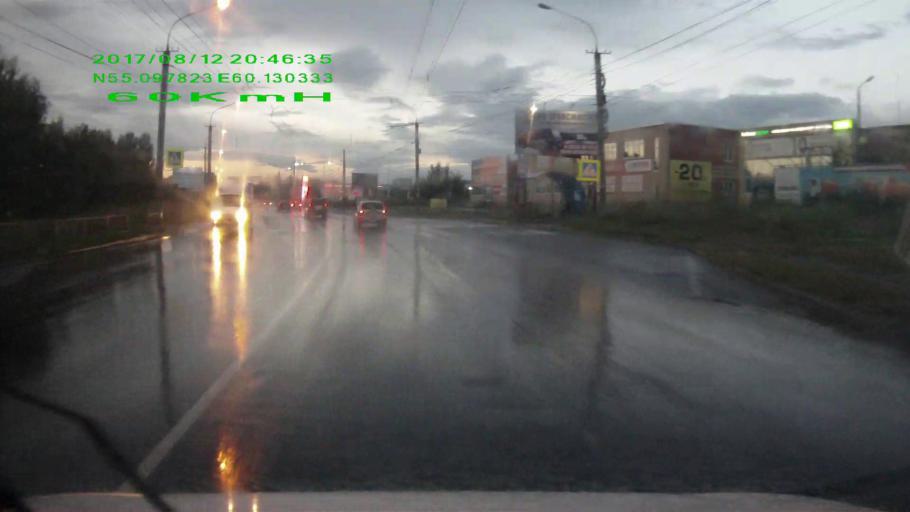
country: RU
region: Chelyabinsk
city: Turgoyak
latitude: 55.0979
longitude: 60.1305
